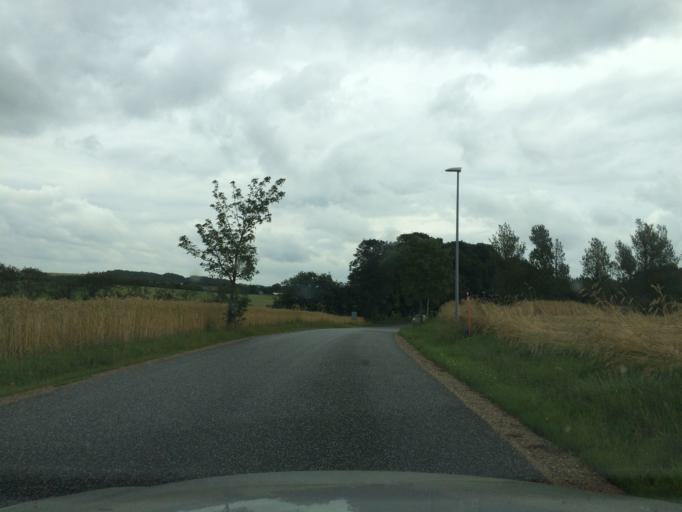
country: DK
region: Central Jutland
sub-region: Skanderborg Kommune
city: Ry
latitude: 56.2166
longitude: 9.7399
